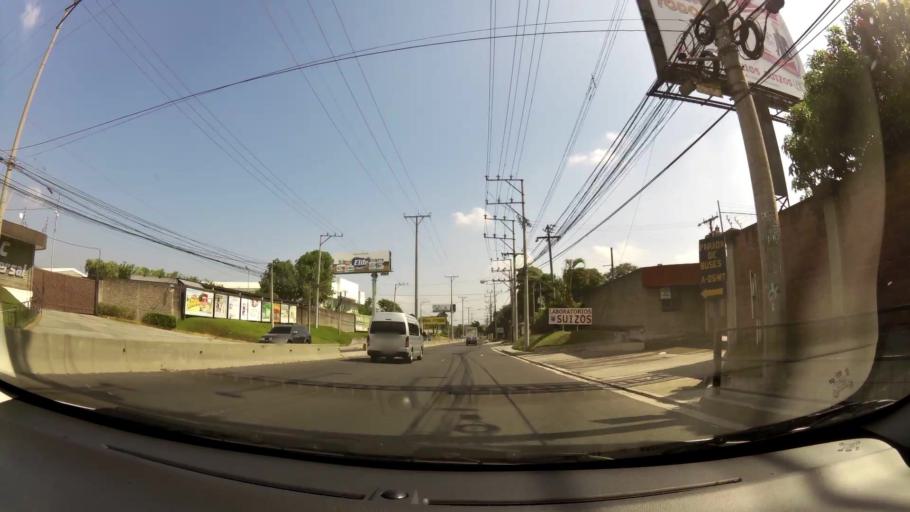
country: SV
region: La Libertad
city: Santa Tecla
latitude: 13.6680
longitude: -89.2691
